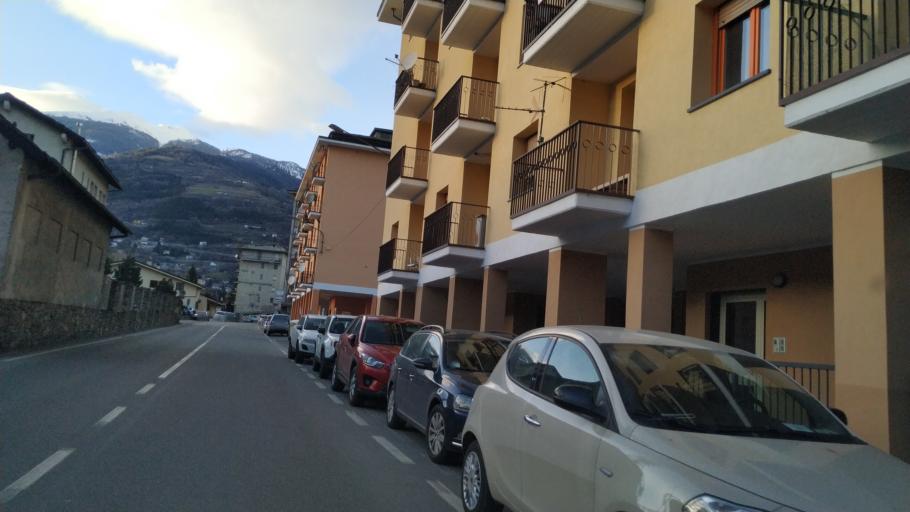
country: IT
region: Aosta Valley
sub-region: Valle d'Aosta
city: Aosta
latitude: 45.7378
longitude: 7.3324
